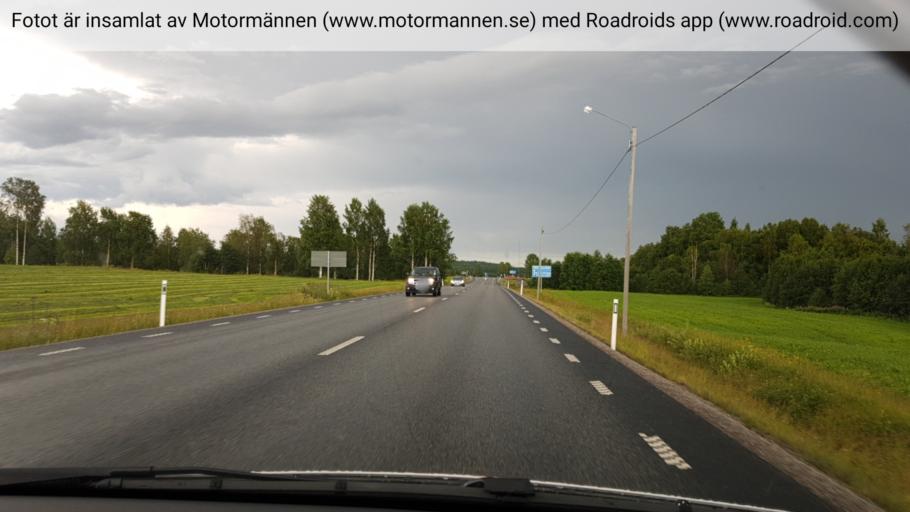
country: SE
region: Vaesterbotten
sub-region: Umea Kommun
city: Roback
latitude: 63.8777
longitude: 20.0559
